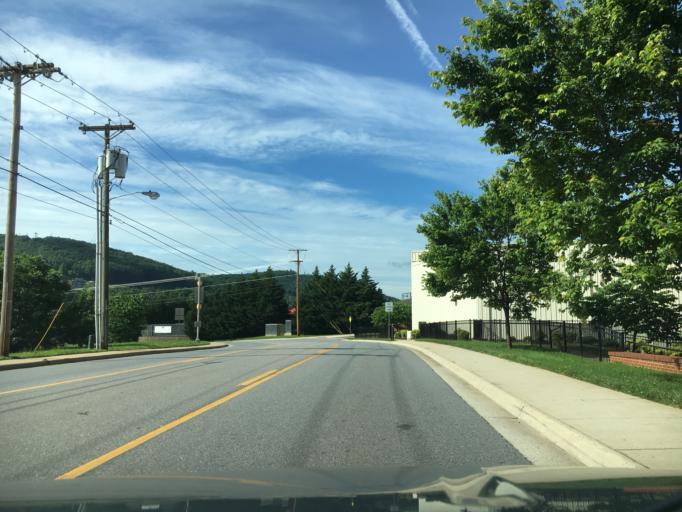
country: US
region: Virginia
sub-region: City of Lynchburg
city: West Lynchburg
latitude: 37.3599
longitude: -79.1719
